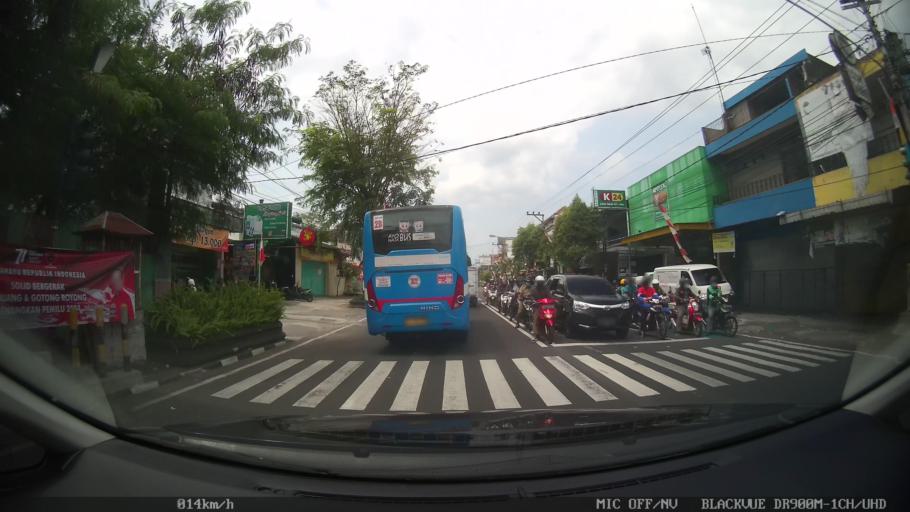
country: ID
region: Daerah Istimewa Yogyakarta
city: Yogyakarta
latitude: -7.8020
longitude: 110.3891
